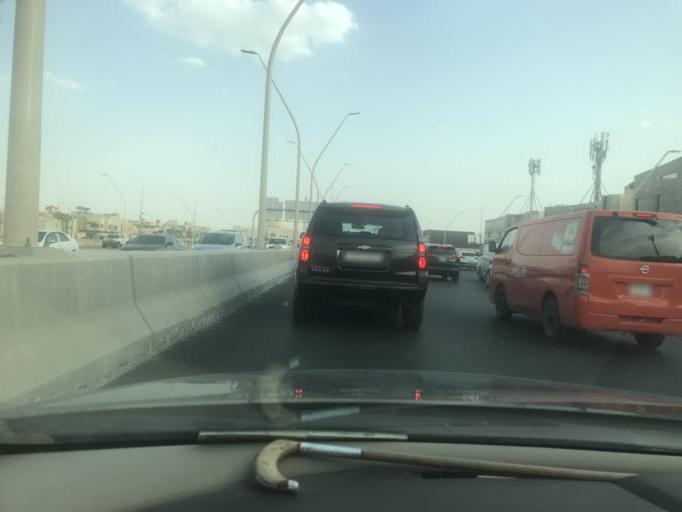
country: SA
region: Ar Riyad
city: Riyadh
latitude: 24.8004
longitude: 46.6748
